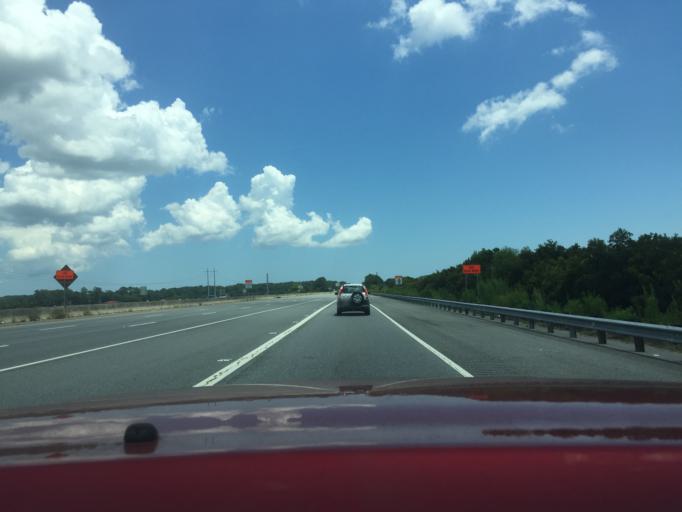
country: US
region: Georgia
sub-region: Chatham County
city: Georgetown
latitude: 31.9841
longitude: -81.1949
